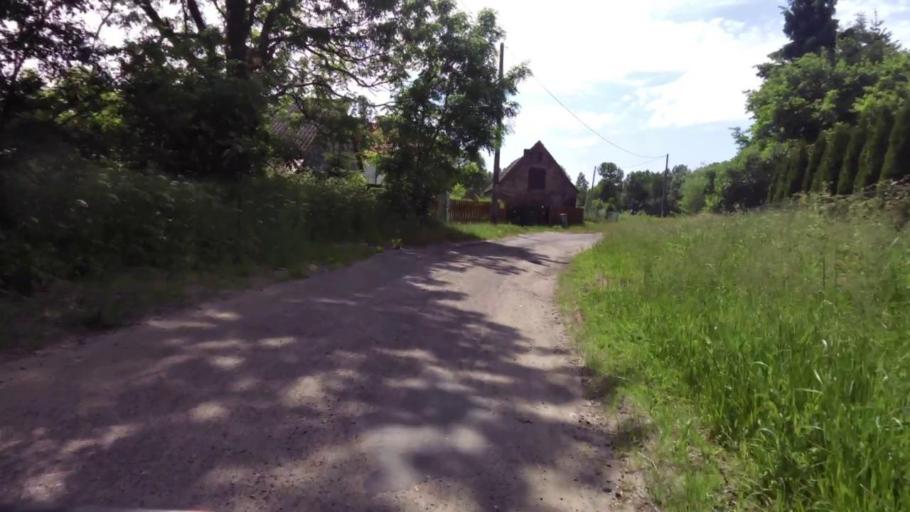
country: PL
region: West Pomeranian Voivodeship
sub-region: Powiat kamienski
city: Wolin
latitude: 53.8501
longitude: 14.5809
